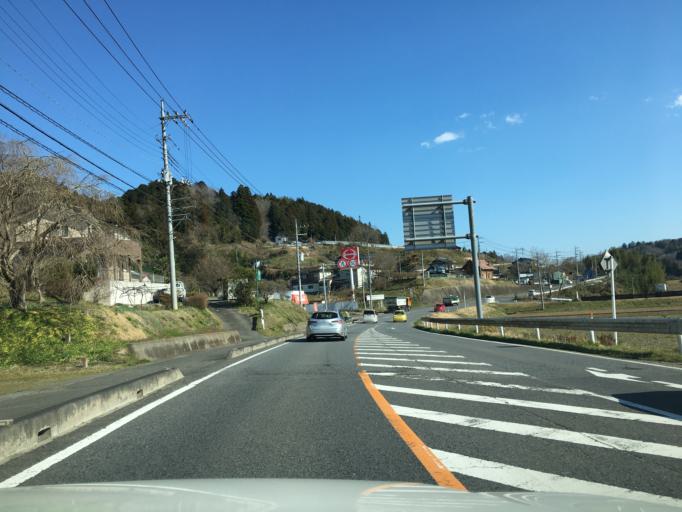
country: JP
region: Tochigi
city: Motegi
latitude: 36.5662
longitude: 140.2841
